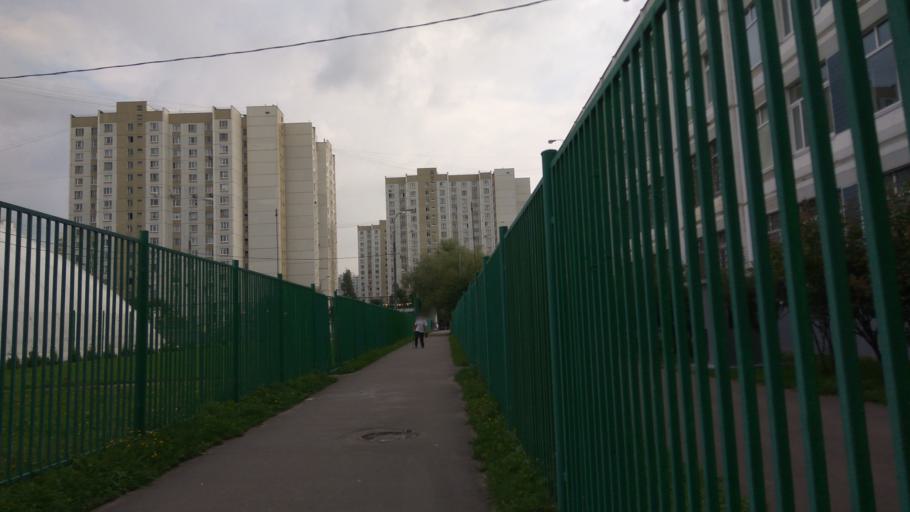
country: RU
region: Moscow
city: Brateyevo
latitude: 55.6356
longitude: 37.7439
